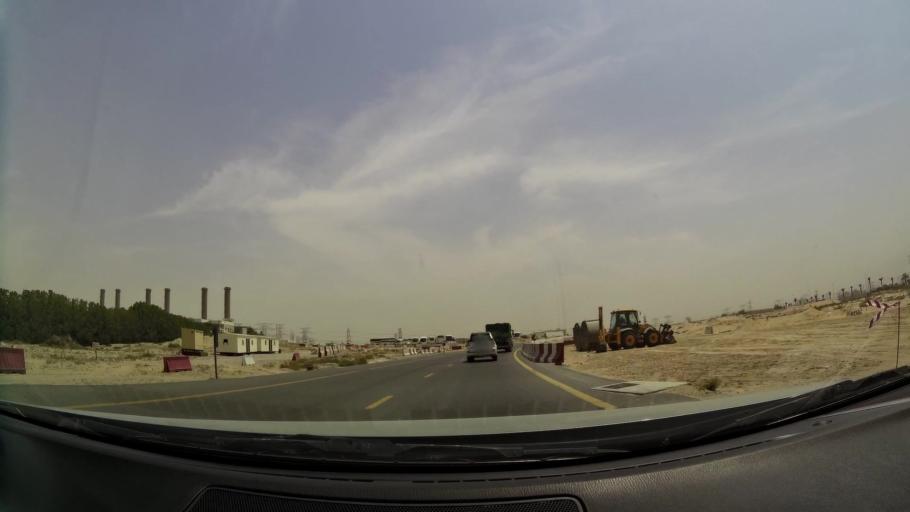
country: AE
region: Ash Shariqah
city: Sharjah
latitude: 25.1544
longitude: 55.4234
